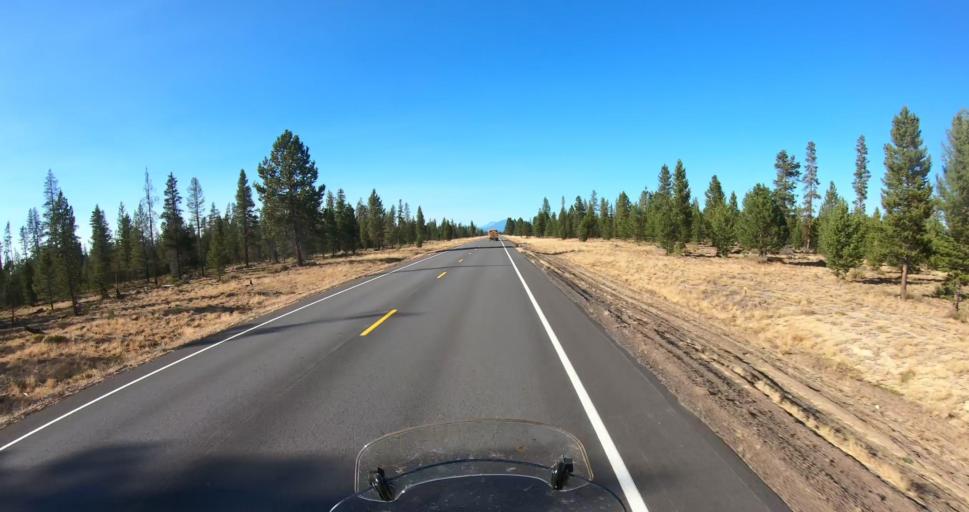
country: US
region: Oregon
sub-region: Deschutes County
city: La Pine
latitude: 43.5961
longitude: -121.4954
